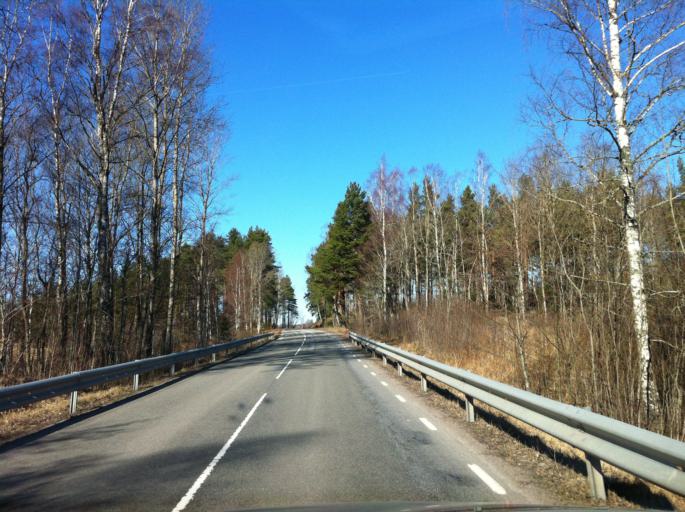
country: SE
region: Vaestra Goetaland
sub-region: Toreboda Kommun
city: Toereboda
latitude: 58.6871
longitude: 14.1111
